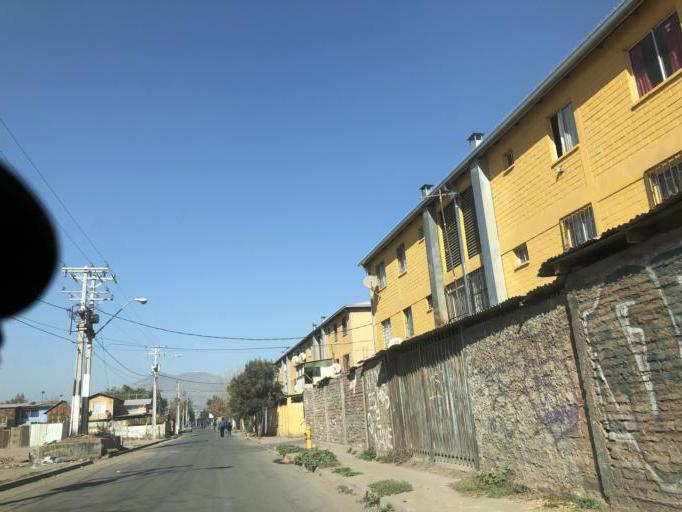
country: CL
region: Santiago Metropolitan
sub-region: Provincia de Santiago
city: La Pintana
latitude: -33.6264
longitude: -70.6265
